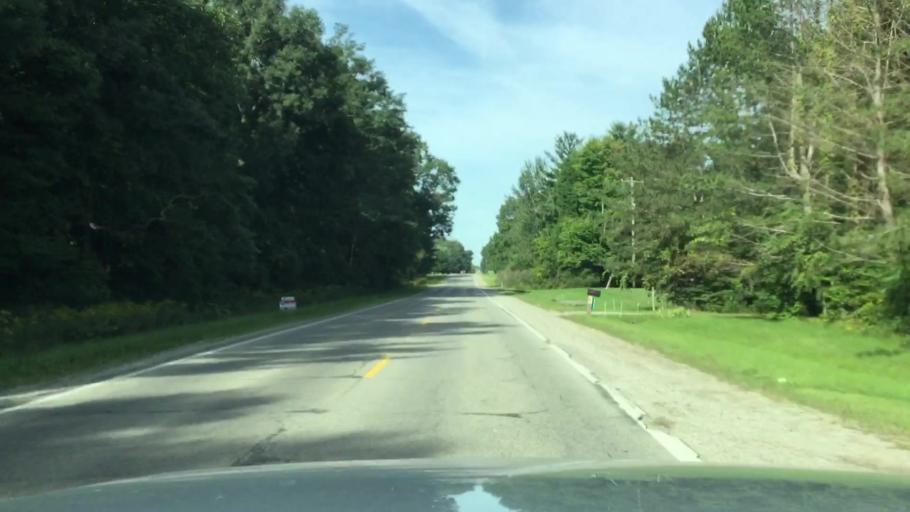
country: US
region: Michigan
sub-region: Genesee County
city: Flushing
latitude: 43.1179
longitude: -83.8356
